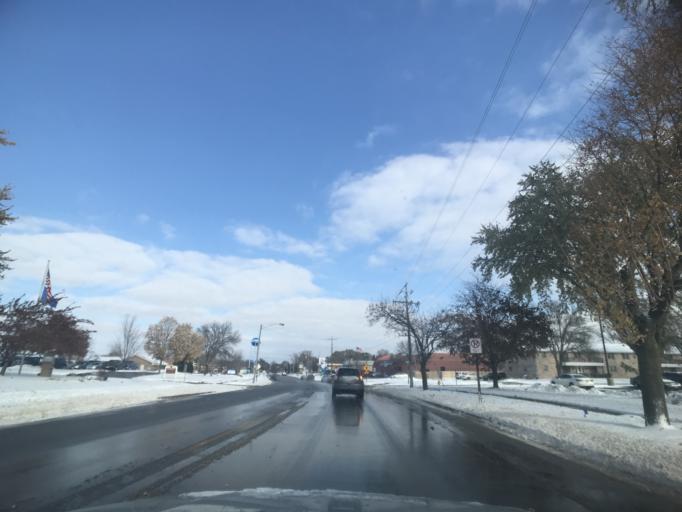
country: US
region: Wisconsin
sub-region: Brown County
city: De Pere
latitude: 44.4484
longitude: -88.0850
